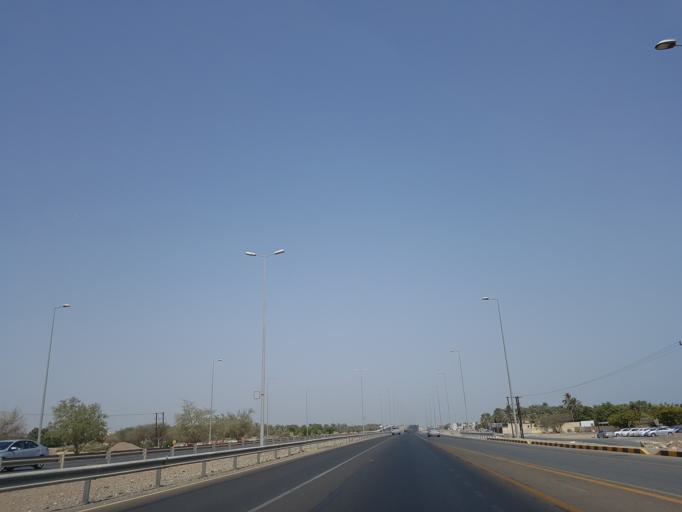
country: OM
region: Al Batinah
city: Saham
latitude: 24.0693
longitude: 56.9520
